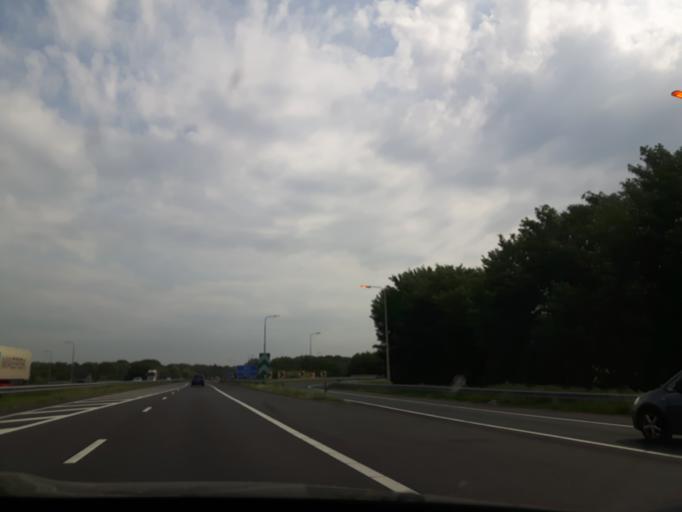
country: NL
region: North Brabant
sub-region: Gemeente Bergen op Zoom
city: Bergen op Zoom
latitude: 51.5016
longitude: 4.3137
